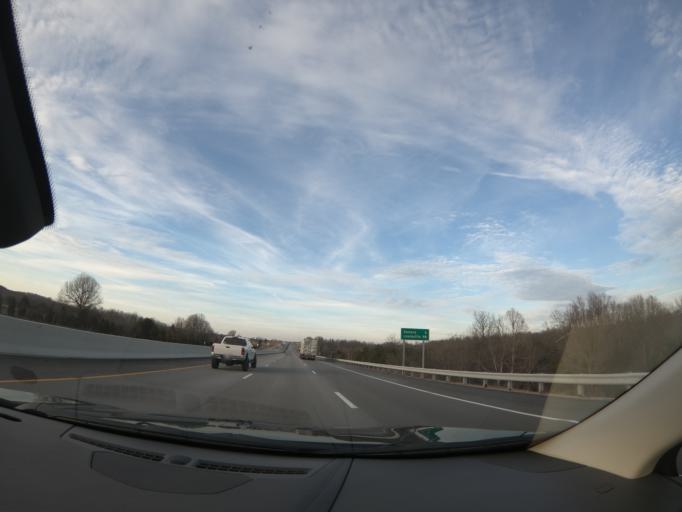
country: US
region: Kentucky
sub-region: Larue County
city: Hodgenville
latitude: 37.4735
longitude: -85.8814
